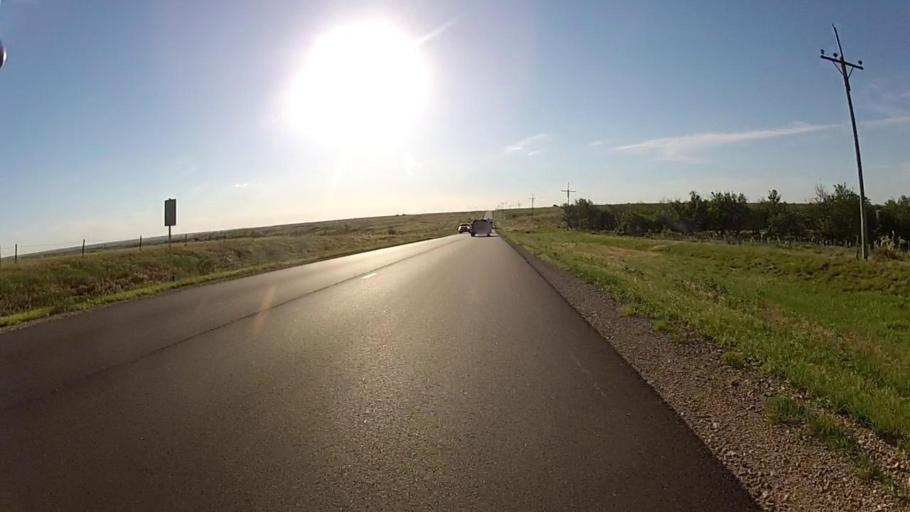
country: US
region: Kansas
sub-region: Comanche County
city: Coldwater
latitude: 37.2822
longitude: -99.1320
